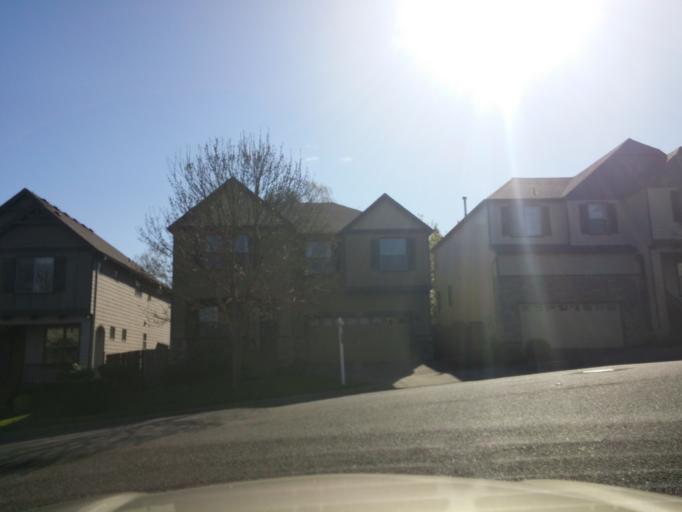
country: US
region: Oregon
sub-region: Washington County
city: Cedar Mill
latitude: 45.5370
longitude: -122.7927
